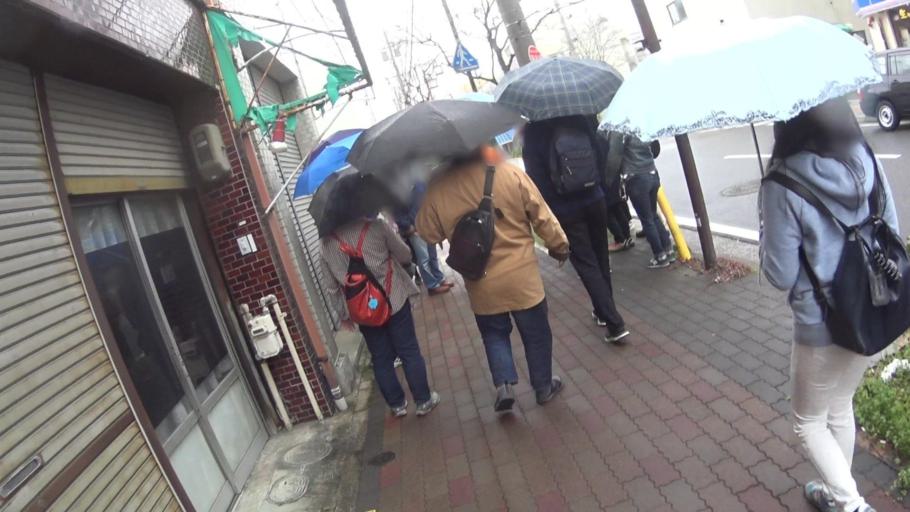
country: JP
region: Aichi
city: Nagoya-shi
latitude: 35.1159
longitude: 136.9071
